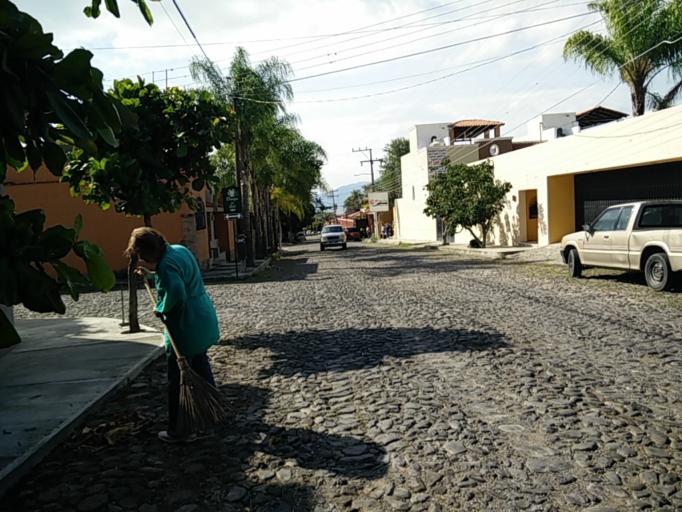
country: MX
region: Jalisco
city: Ajijic
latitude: 20.3003
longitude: -103.2759
